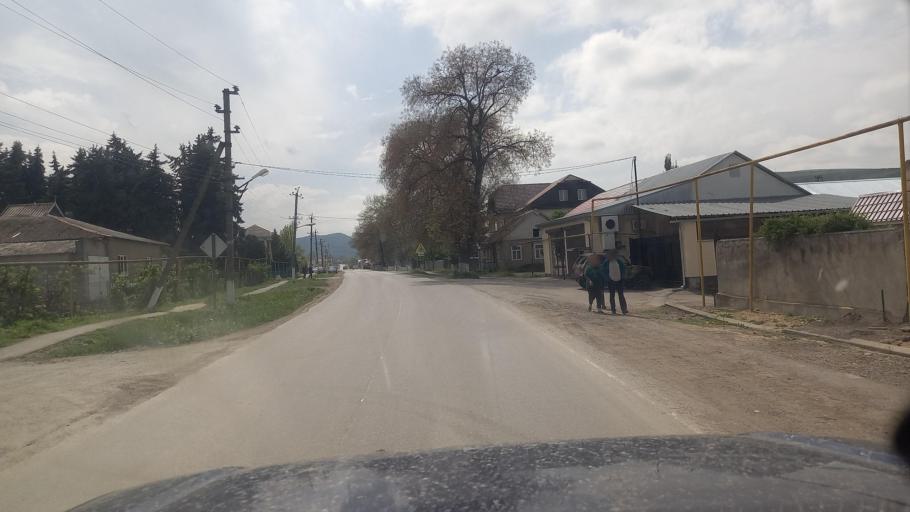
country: RU
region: Kabardino-Balkariya
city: Sarmakovo
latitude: 43.7426
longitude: 43.1943
